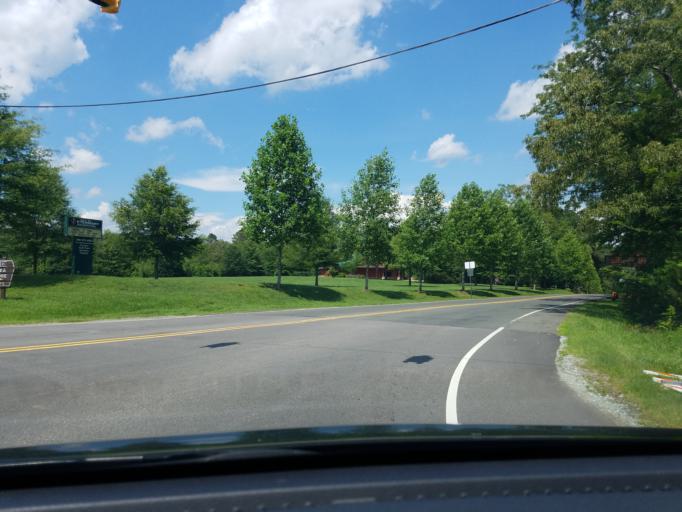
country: US
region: North Carolina
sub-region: Durham County
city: Gorman
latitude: 36.1512
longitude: -78.9054
